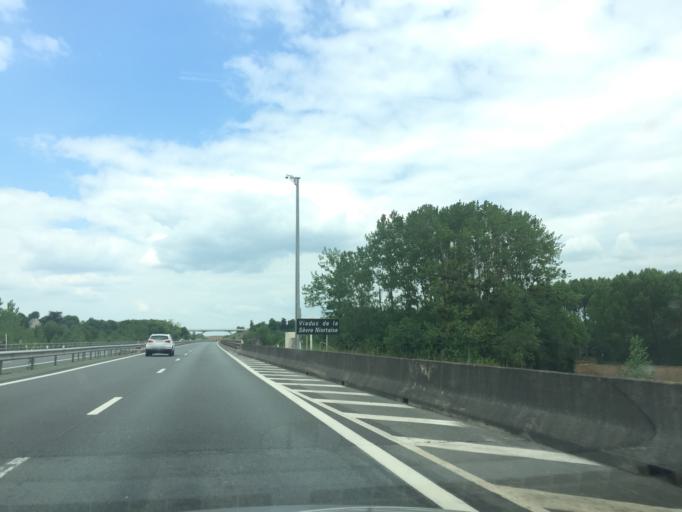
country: FR
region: Poitou-Charentes
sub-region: Departement des Deux-Sevres
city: Chauray
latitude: 46.3741
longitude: -0.3582
